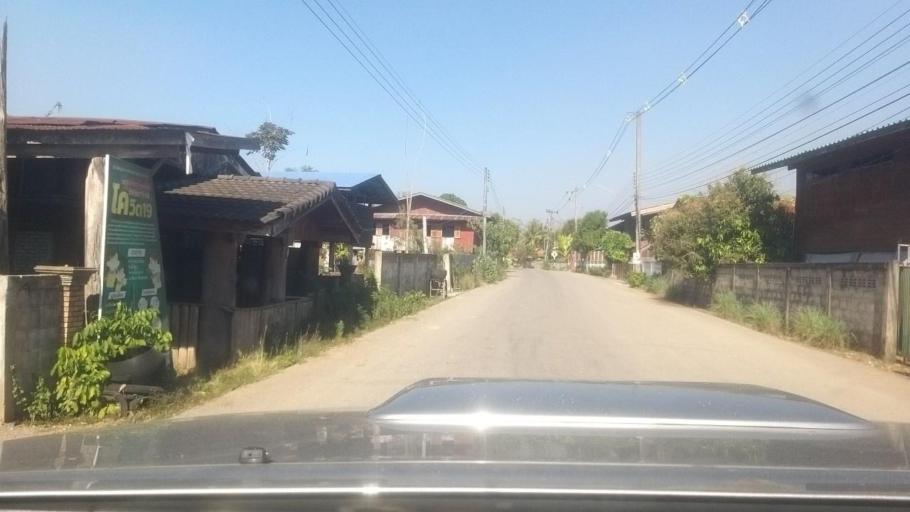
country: TH
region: Phrae
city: Nong Muang Khai
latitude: 18.2977
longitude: 100.0243
